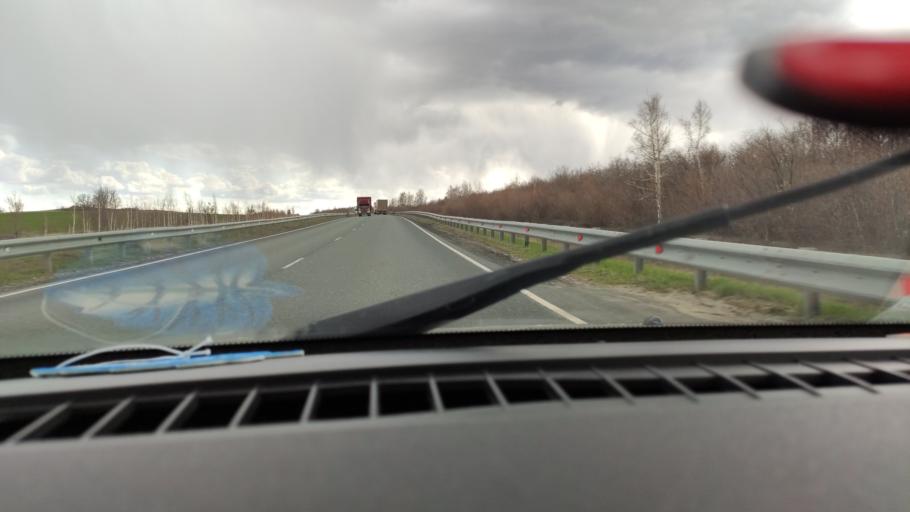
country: RU
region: Saratov
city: Balakovo
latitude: 52.1670
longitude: 47.8267
